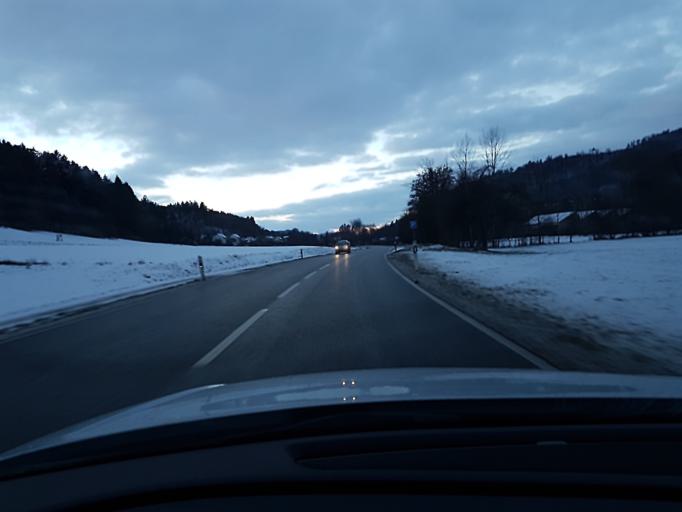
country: DE
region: Baden-Wuerttemberg
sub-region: Regierungsbezirk Stuttgart
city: Murrhardt
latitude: 48.9726
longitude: 9.6136
